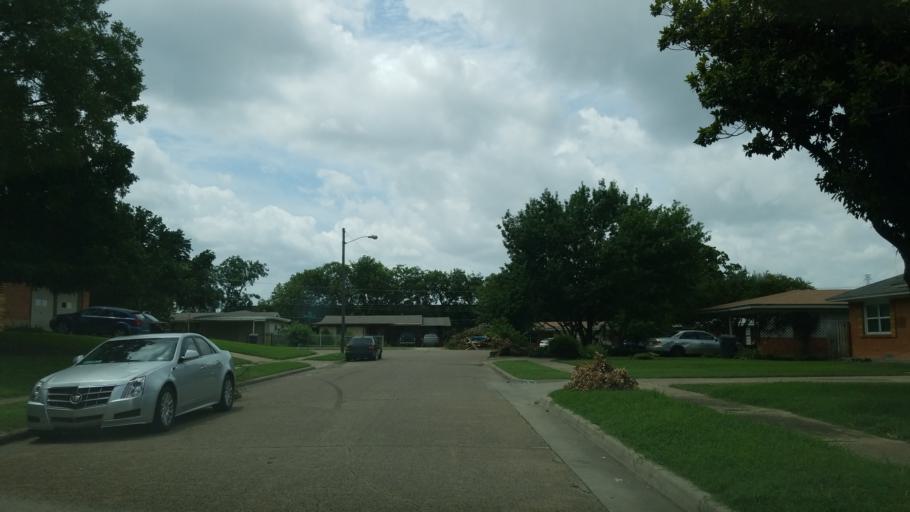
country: US
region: Texas
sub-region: Dallas County
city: Farmers Branch
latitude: 32.8884
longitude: -96.8816
